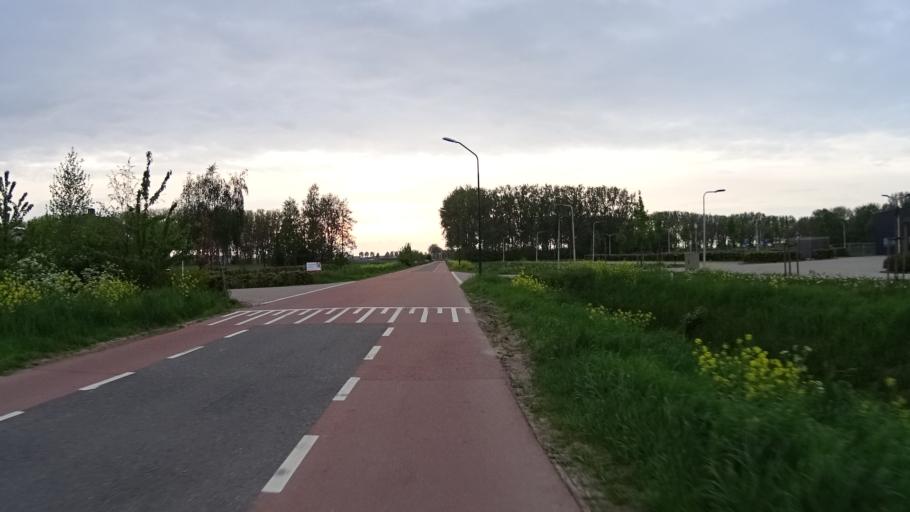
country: NL
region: North Brabant
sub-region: Gemeente Woudrichem
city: Woudrichem
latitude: 51.7764
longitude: 5.0564
